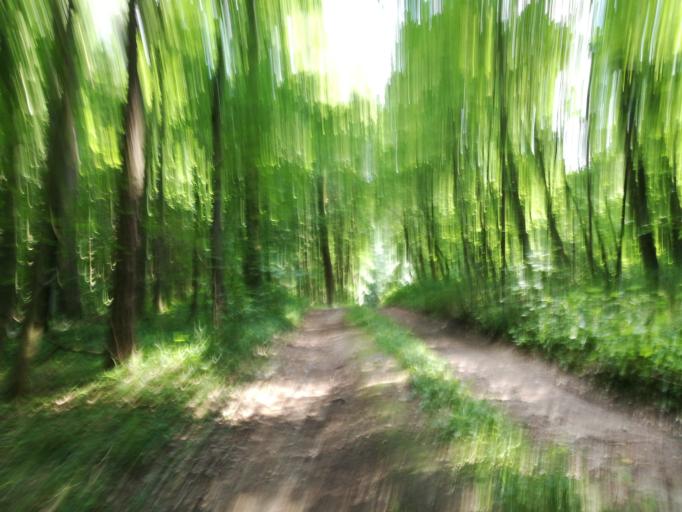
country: DE
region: Bavaria
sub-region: Regierungsbezirk Mittelfranken
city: Obermichelbach
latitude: 49.5055
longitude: 10.9192
